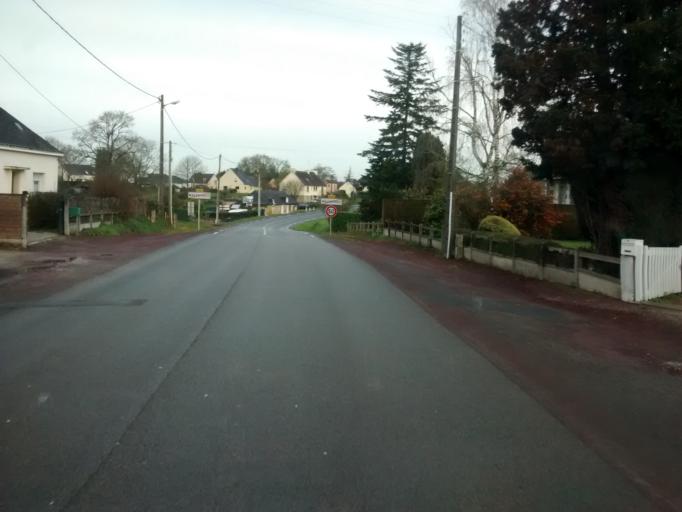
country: FR
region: Brittany
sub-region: Departement du Morbihan
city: Malestroit
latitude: 47.8187
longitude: -2.3764
